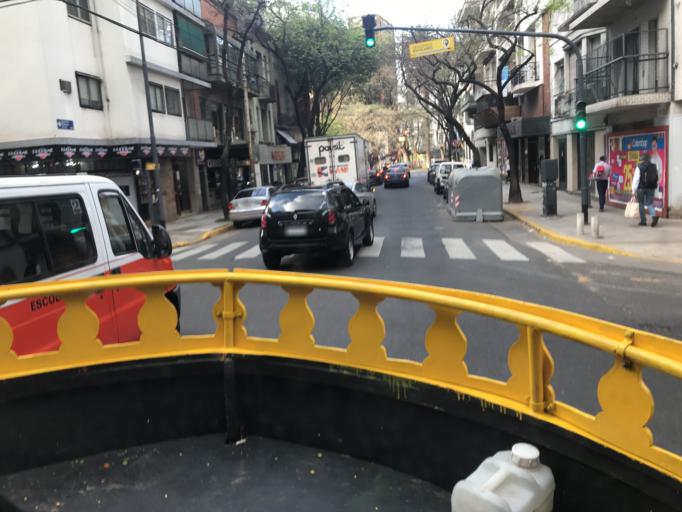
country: AR
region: Buenos Aires F.D.
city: Retiro
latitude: -34.5905
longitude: -58.4171
